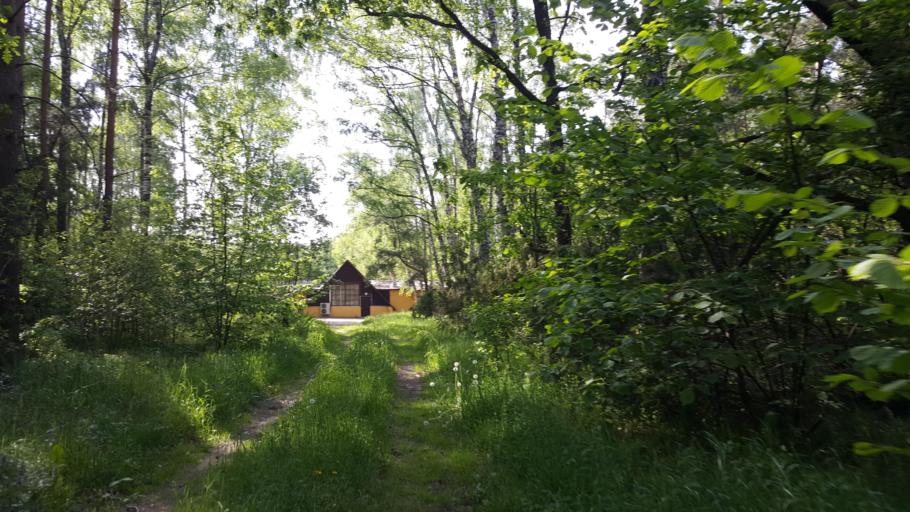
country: BY
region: Brest
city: Kamyanyets
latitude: 52.3508
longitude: 23.7850
